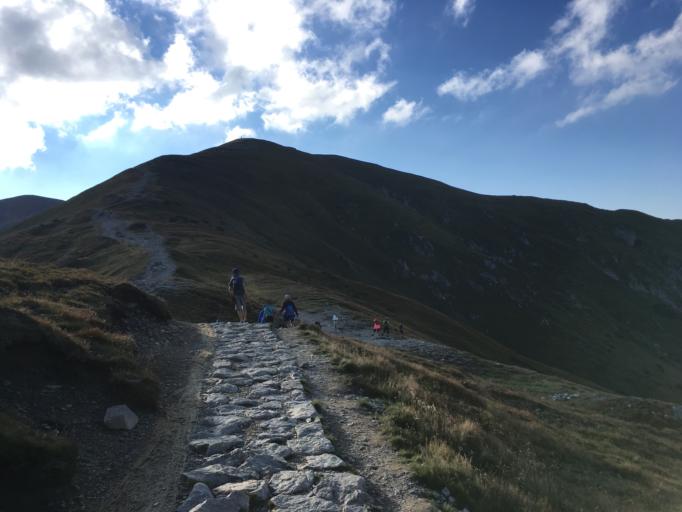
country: PL
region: Lesser Poland Voivodeship
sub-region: Powiat tatrzanski
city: Zakopane
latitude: 49.2342
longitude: 19.9394
